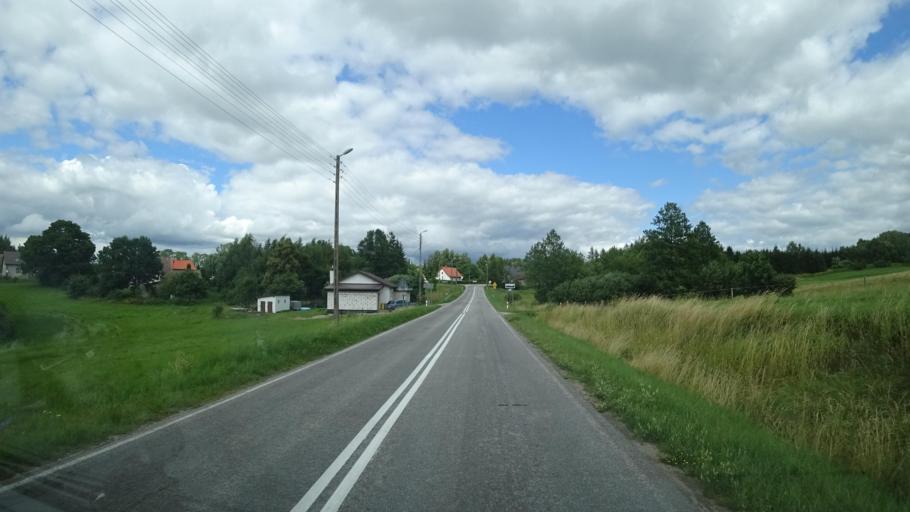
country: PL
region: Warmian-Masurian Voivodeship
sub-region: Powiat goldapski
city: Goldap
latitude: 54.2231
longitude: 22.2338
